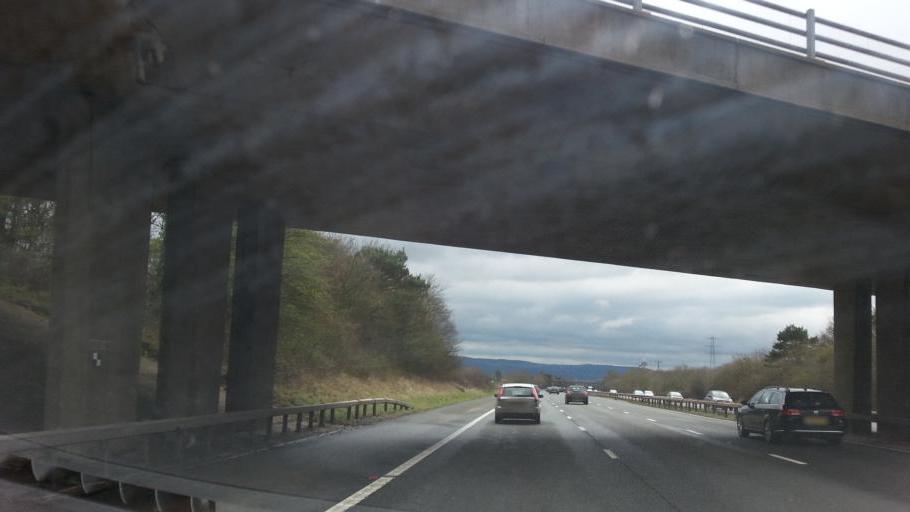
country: GB
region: England
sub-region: Somerset
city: Creech Saint Michael
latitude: 51.0482
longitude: -3.0284
